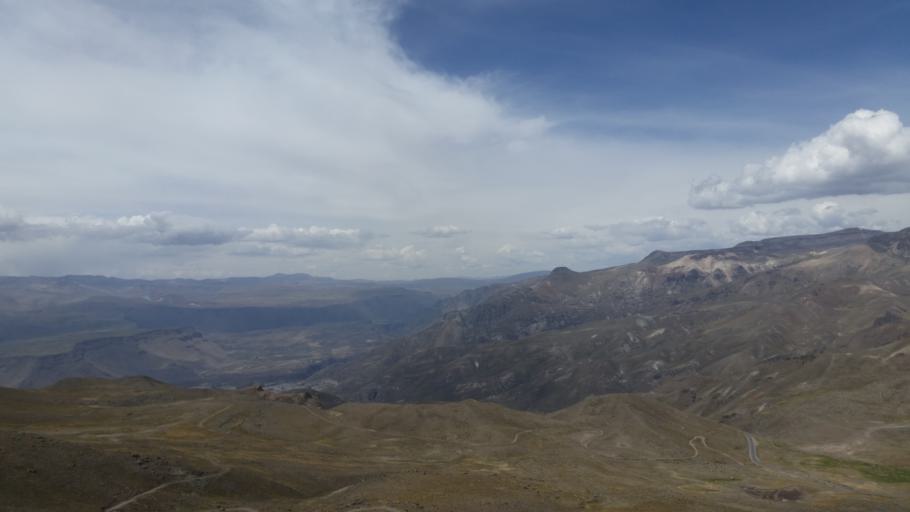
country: PE
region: Arequipa
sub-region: Provincia de Caylloma
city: Chivay
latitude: -15.7052
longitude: -71.6032
